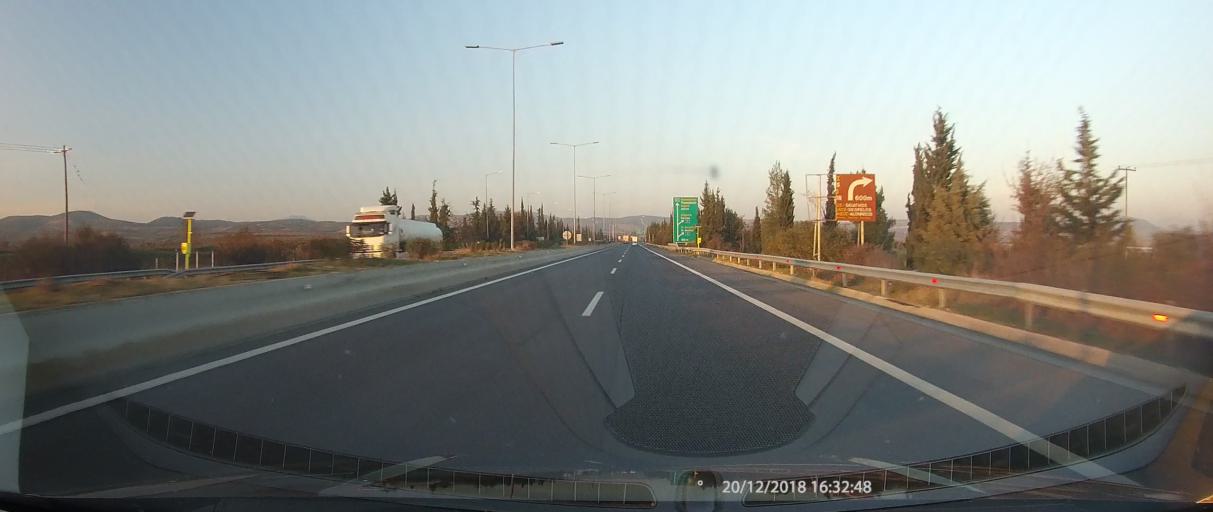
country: GR
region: Thessaly
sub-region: Nomos Magnisias
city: Evxinoupolis
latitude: 39.2516
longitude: 22.7353
